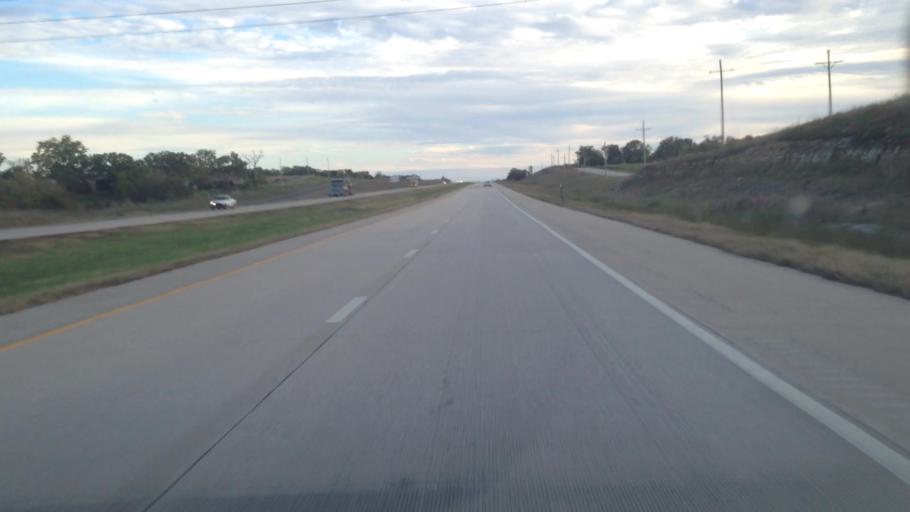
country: US
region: Kansas
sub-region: Douglas County
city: Baldwin City
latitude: 38.8168
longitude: -95.2692
